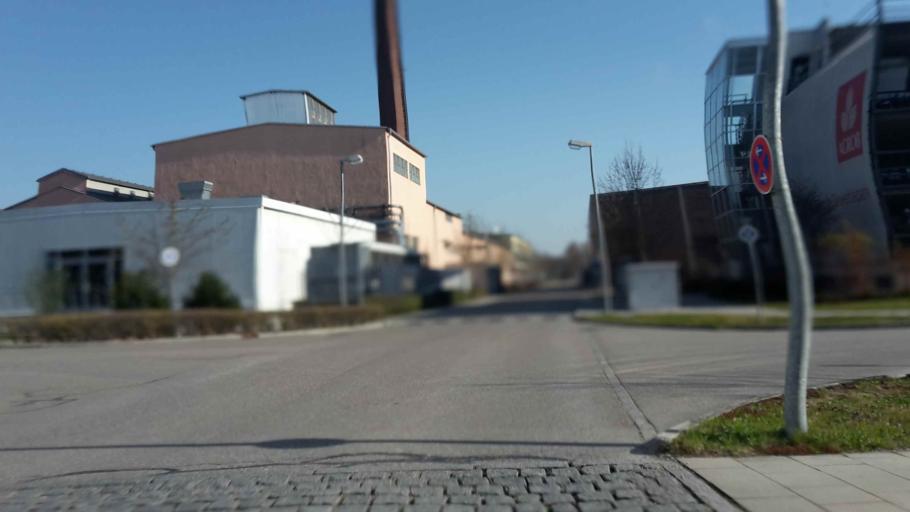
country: DE
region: Bavaria
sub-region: Upper Bavaria
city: Unterfoehring
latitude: 48.2083
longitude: 11.6587
